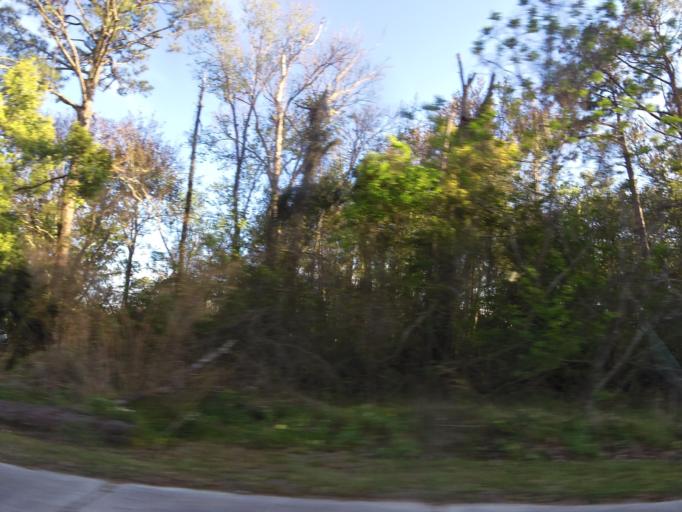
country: US
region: Florida
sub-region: Duval County
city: Jacksonville
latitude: 30.4678
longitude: -81.6199
